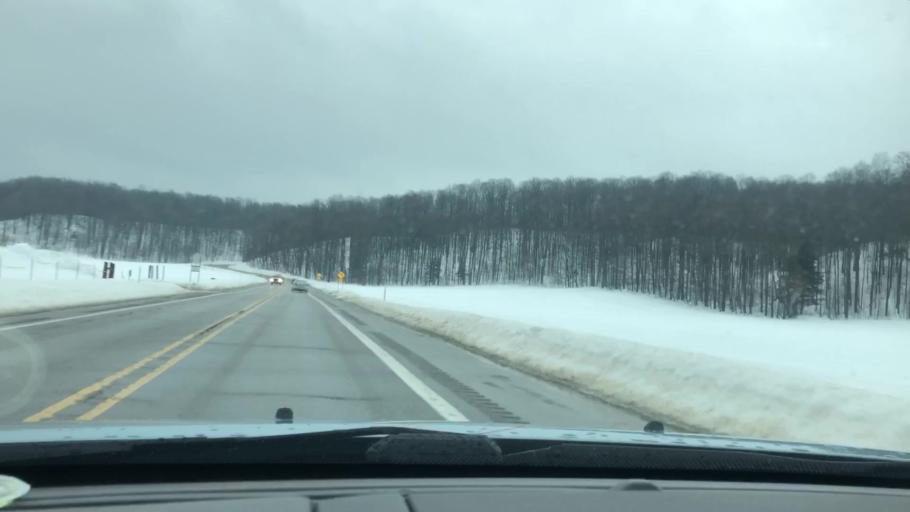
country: US
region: Michigan
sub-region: Charlevoix County
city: Boyne City
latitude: 45.0812
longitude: -84.9185
